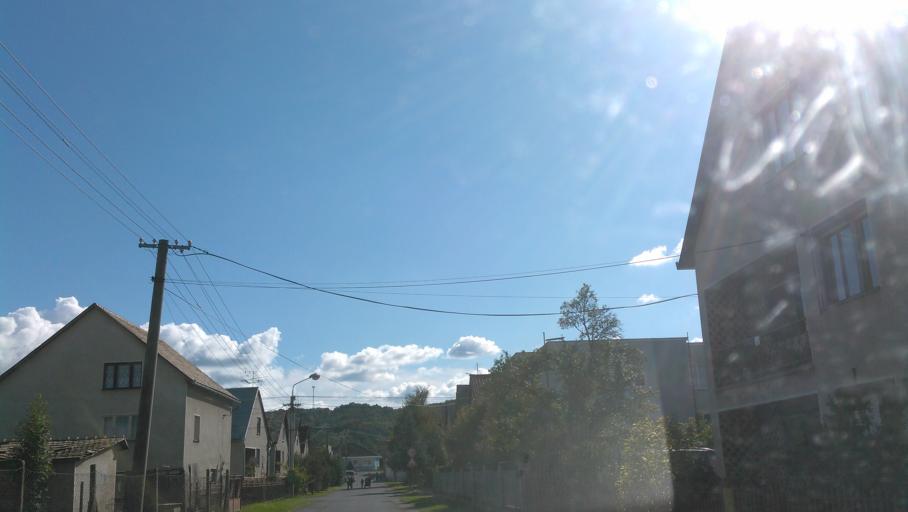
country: SK
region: Banskobystricky
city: Poltar
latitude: 48.3790
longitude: 19.8902
